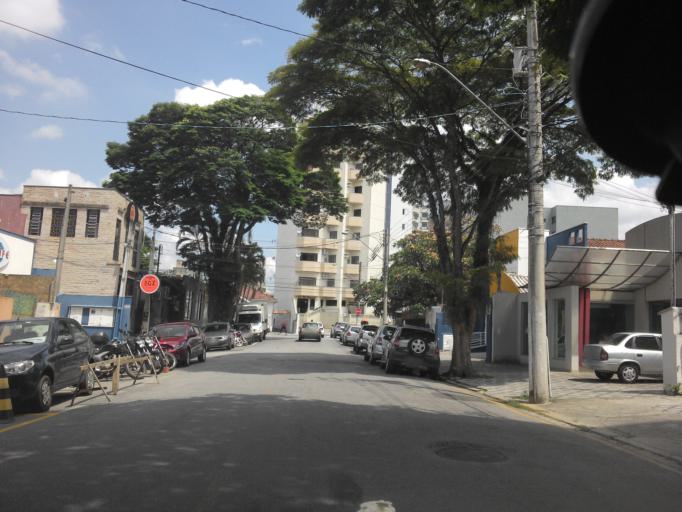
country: BR
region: Sao Paulo
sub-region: Taubate
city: Taubate
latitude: -23.0224
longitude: -45.5557
